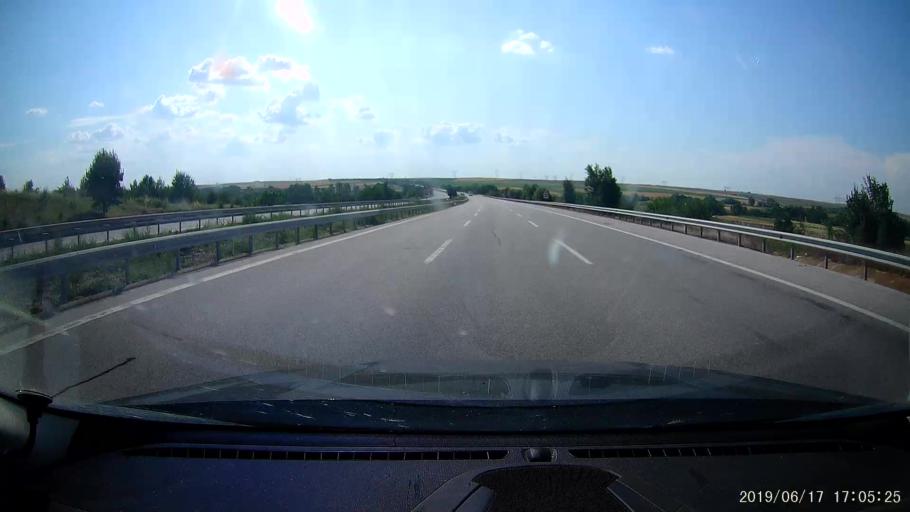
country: TR
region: Edirne
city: Edirne
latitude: 41.6596
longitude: 26.6998
